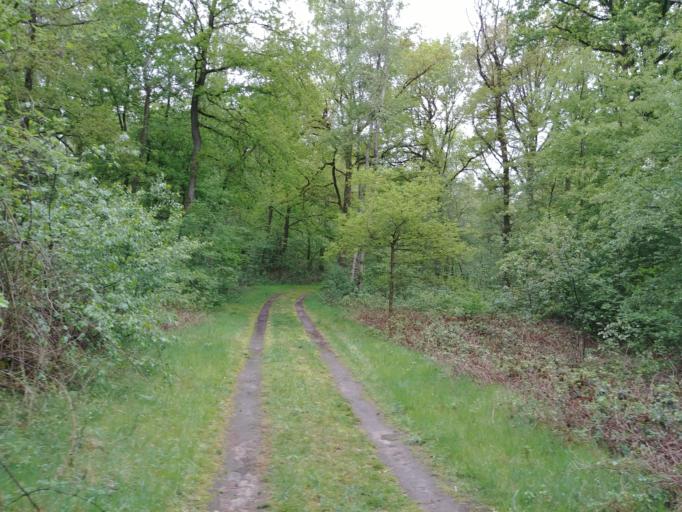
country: NL
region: Overijssel
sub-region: Gemeente Dalfsen
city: Dalfsen
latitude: 52.5187
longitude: 6.3553
